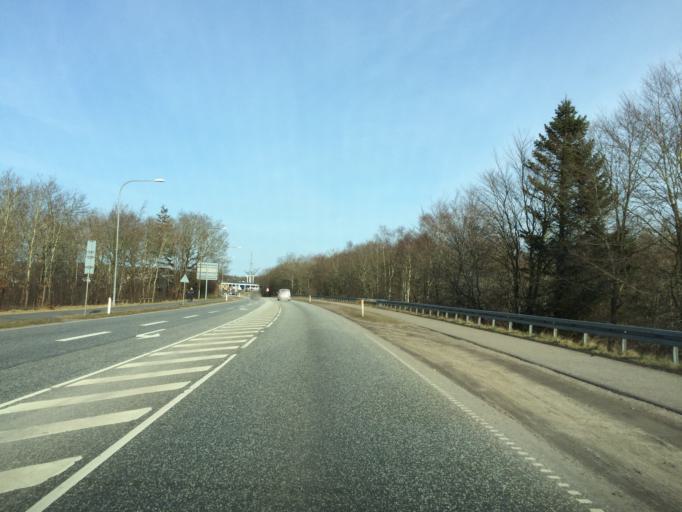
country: DK
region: Central Jutland
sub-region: Holstebro Kommune
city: Holstebro
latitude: 56.3466
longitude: 8.6329
